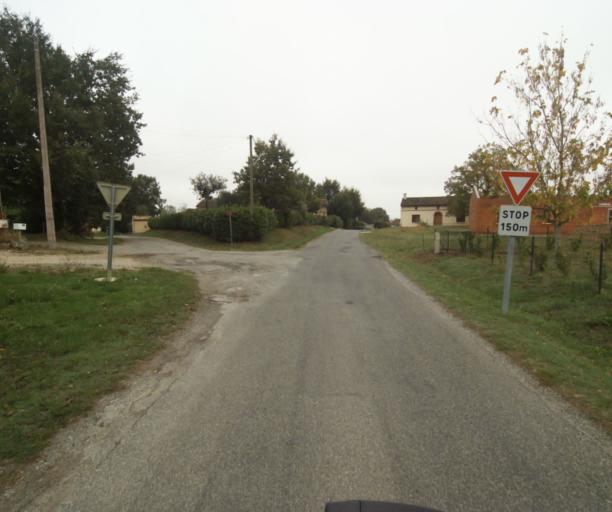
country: FR
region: Midi-Pyrenees
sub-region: Departement du Tarn-et-Garonne
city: Labastide-Saint-Pierre
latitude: 43.8842
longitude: 1.3806
